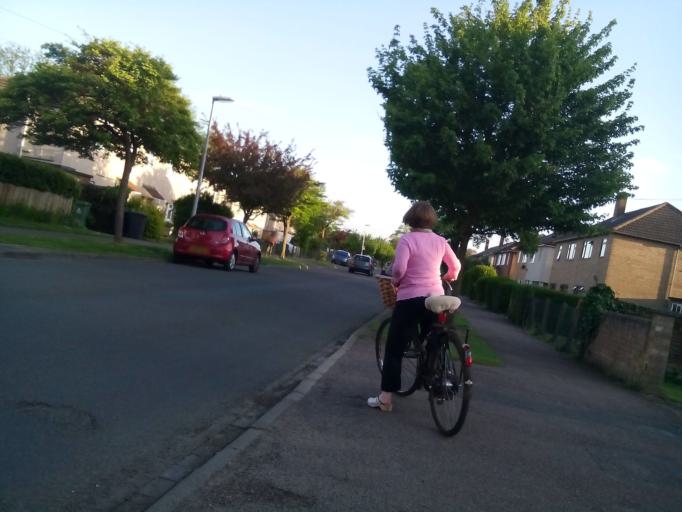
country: GB
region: England
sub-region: Cambridgeshire
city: Cambridge
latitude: 52.1860
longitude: 0.1542
